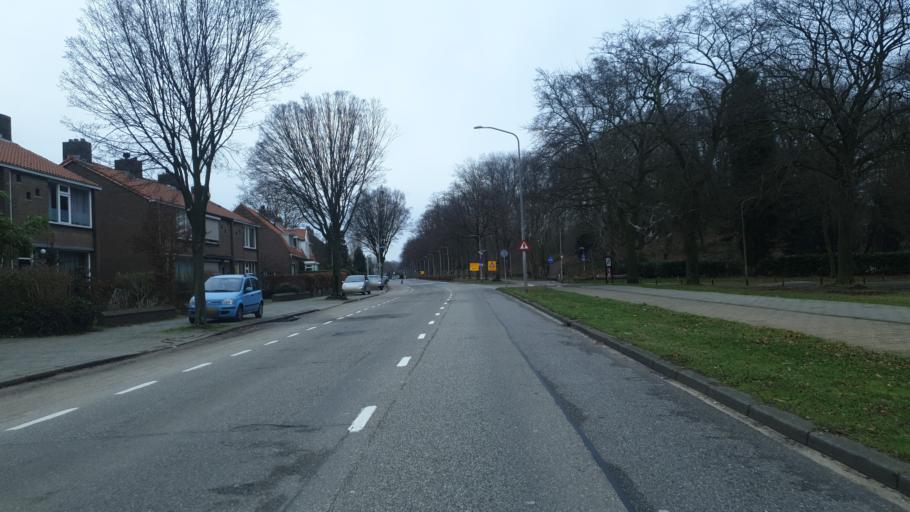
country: NL
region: Gelderland
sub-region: Gemeente Nijmegen
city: Nijmegen
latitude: 51.8269
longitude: 5.8292
